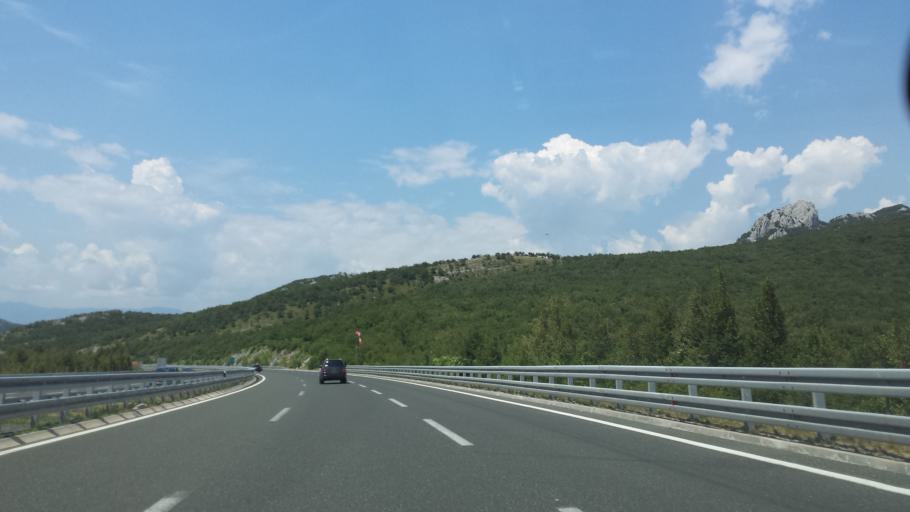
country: HR
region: Primorsko-Goranska
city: Krasica
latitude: 45.3618
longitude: 14.5716
